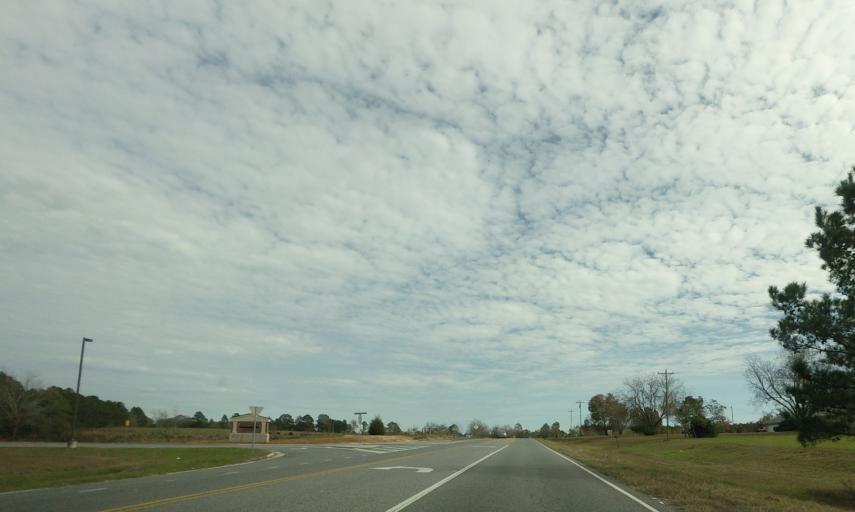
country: US
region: Georgia
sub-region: Bleckley County
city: Cochran
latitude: 32.3974
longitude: -83.3279
